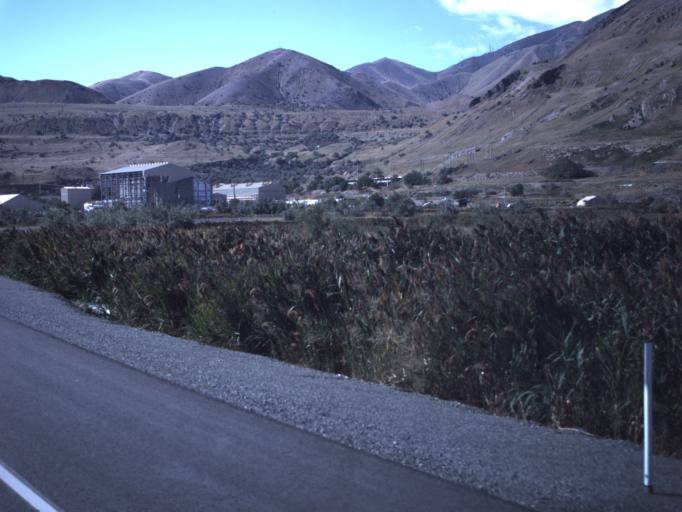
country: US
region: Utah
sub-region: Salt Lake County
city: Magna
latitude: 40.7334
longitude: -112.1694
